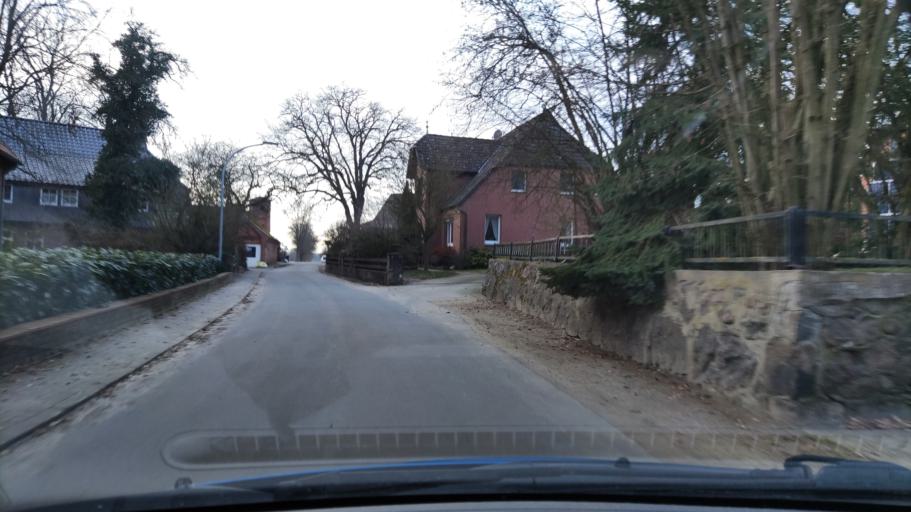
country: DE
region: Lower Saxony
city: Gerdau
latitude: 52.9676
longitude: 10.4180
